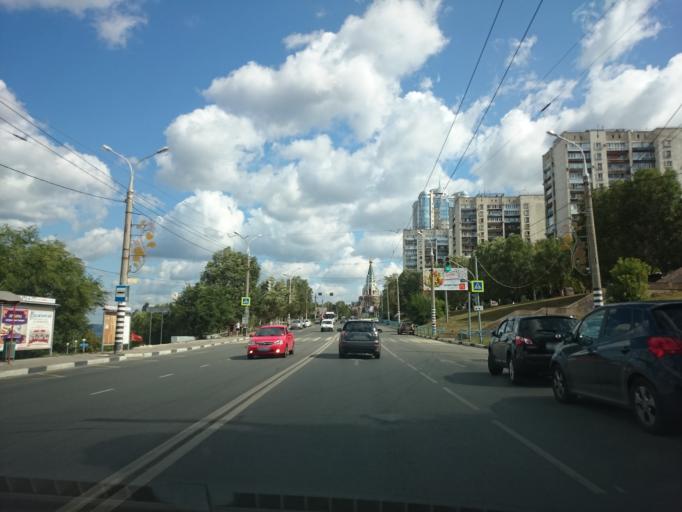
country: RU
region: Samara
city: Samara
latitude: 53.2135
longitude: 50.1286
